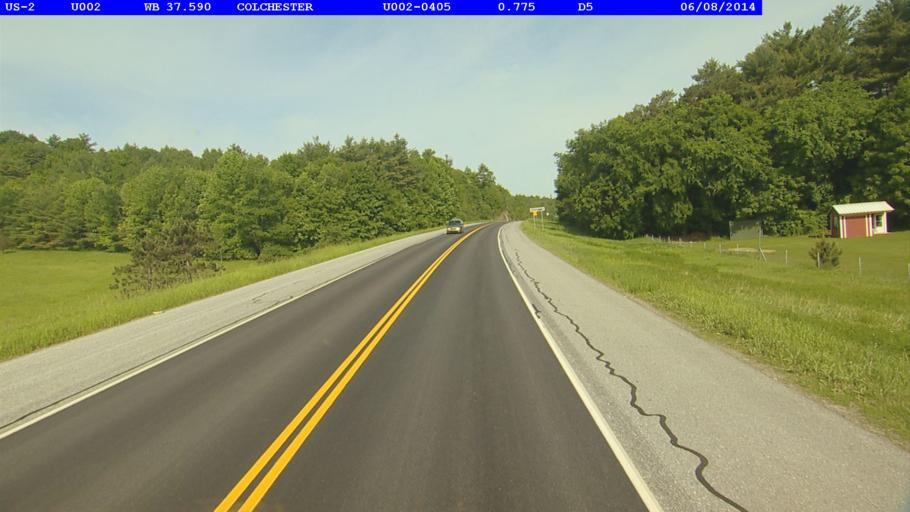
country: US
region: Vermont
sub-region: Chittenden County
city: Colchester
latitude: 44.5959
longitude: -73.1937
